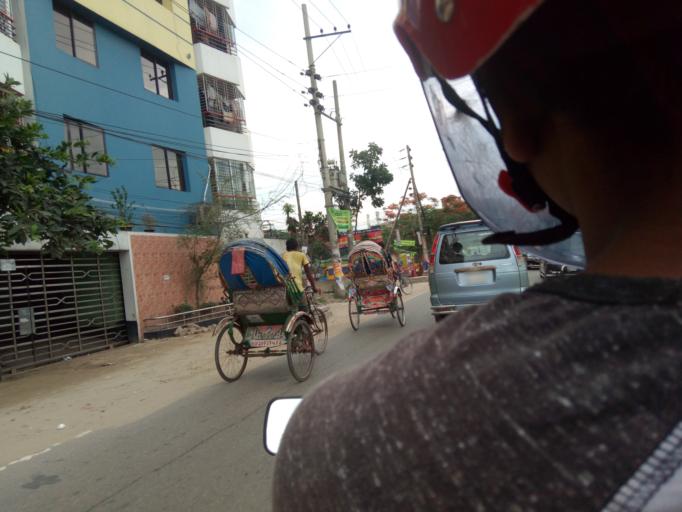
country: BD
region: Dhaka
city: Paltan
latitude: 23.7631
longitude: 90.4340
